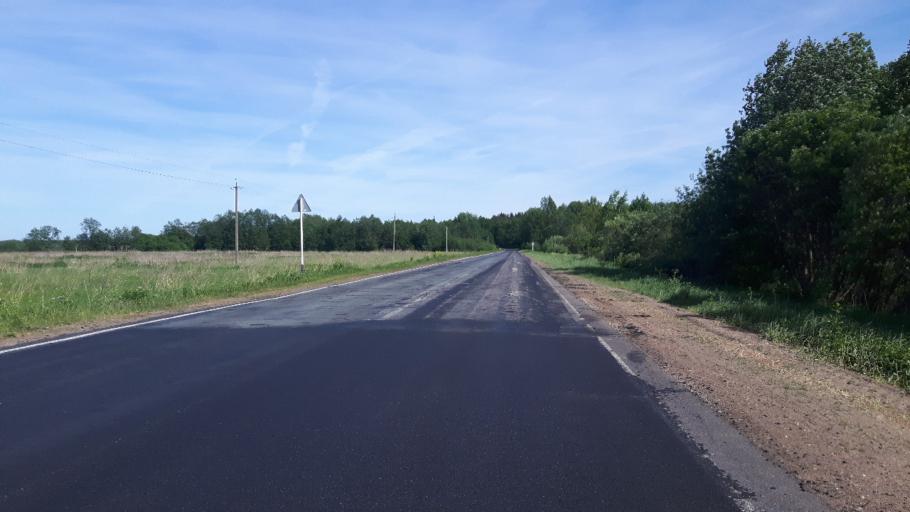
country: RU
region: Leningrad
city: Ivangorod
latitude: 59.4182
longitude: 28.3617
